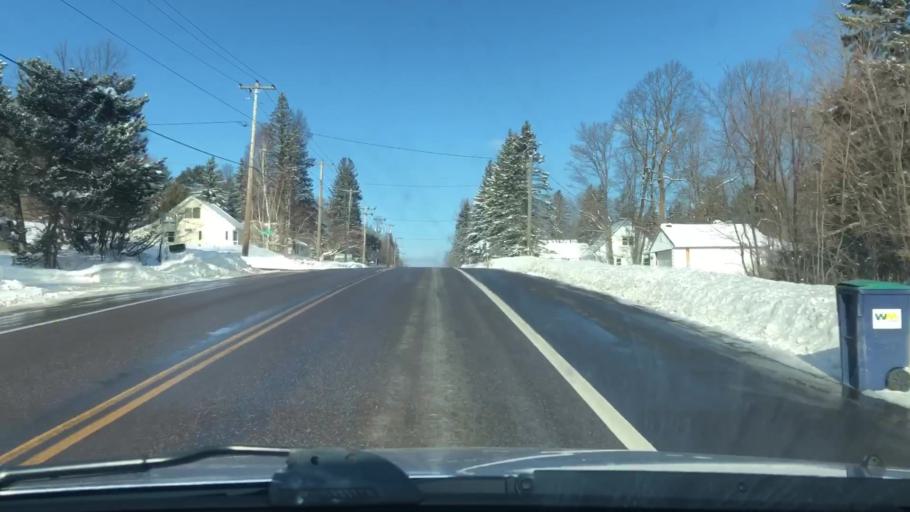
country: US
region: Minnesota
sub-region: Saint Louis County
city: Duluth
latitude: 46.8125
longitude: -92.1322
